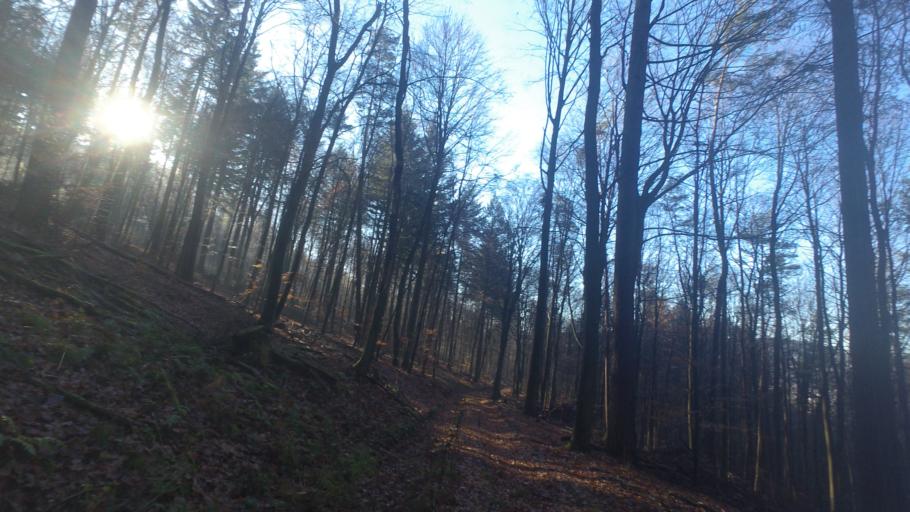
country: DE
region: Baden-Wuerttemberg
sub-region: Karlsruhe Region
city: Heddesbach
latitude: 49.4905
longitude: 8.8124
